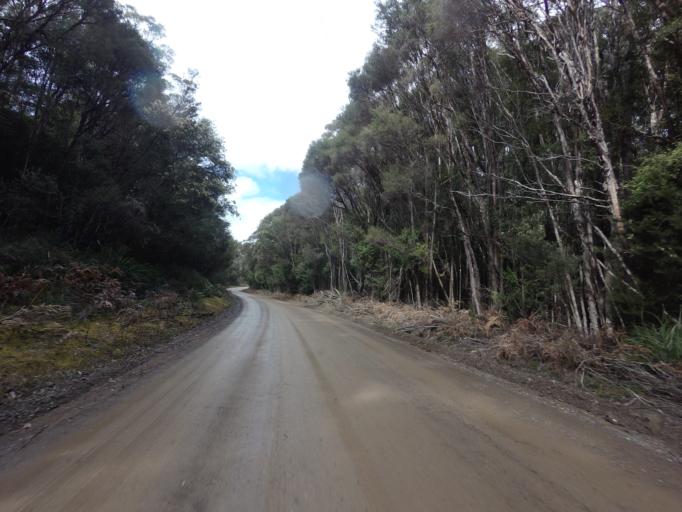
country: AU
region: Tasmania
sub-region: Huon Valley
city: Geeveston
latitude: -43.4053
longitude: 146.8673
